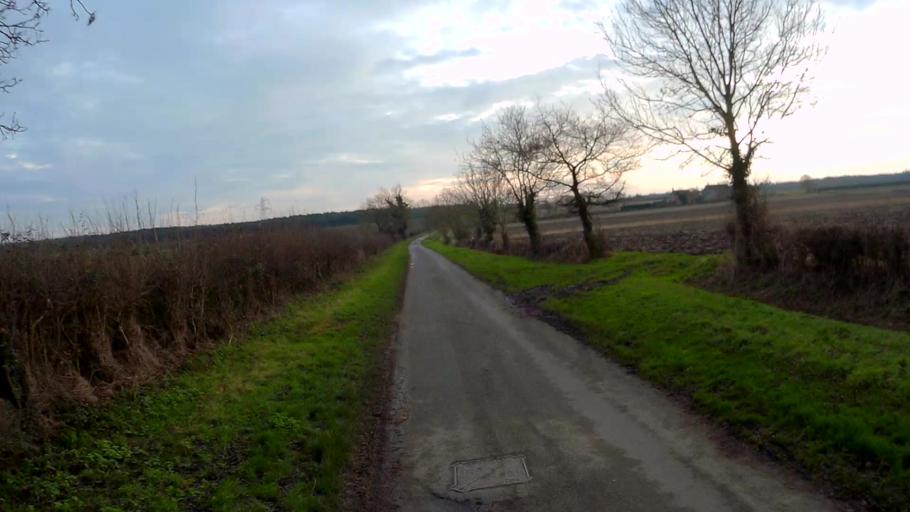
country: GB
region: England
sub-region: Lincolnshire
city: Bourne
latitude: 52.8290
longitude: -0.4056
